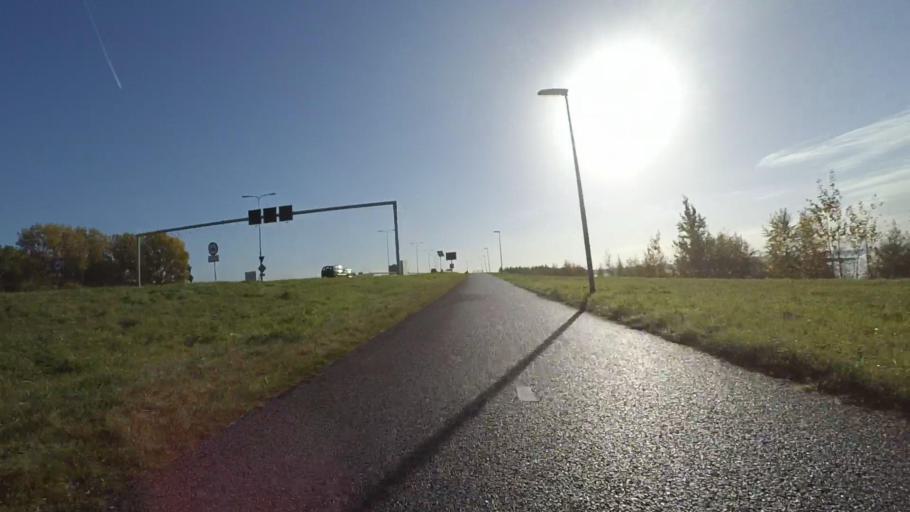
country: NL
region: Gelderland
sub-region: Gemeente Harderwijk
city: Harderwijk
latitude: 52.3655
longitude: 5.6089
